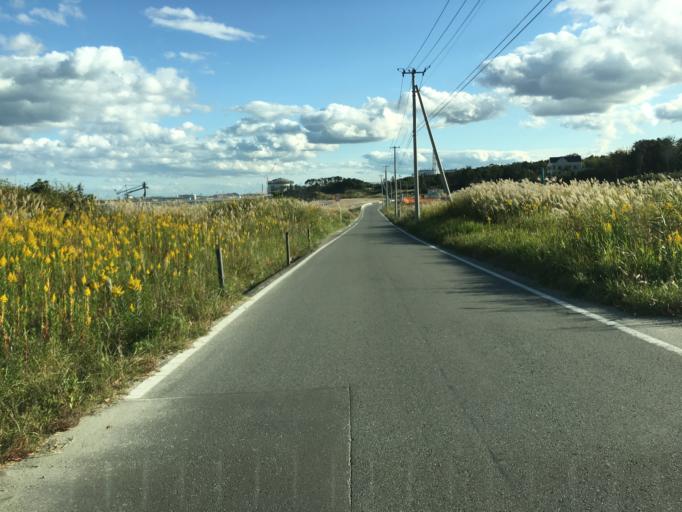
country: JP
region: Miyagi
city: Marumori
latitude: 37.8663
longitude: 140.9388
